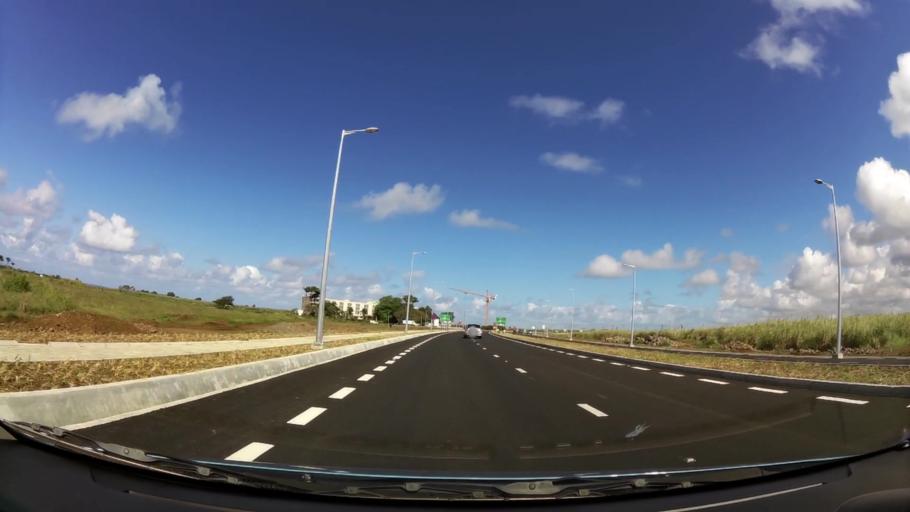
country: MU
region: Grand Port
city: Plaine Magnien
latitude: -20.4373
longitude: 57.6725
